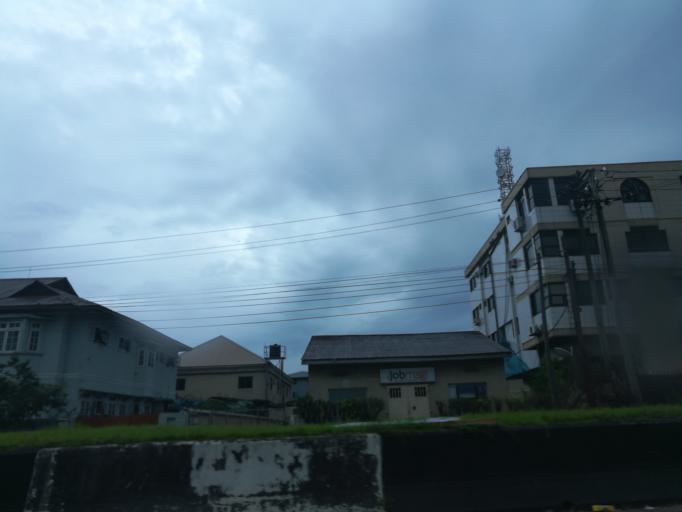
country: NG
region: Lagos
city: Makoko
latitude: 6.5010
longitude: 3.3777
